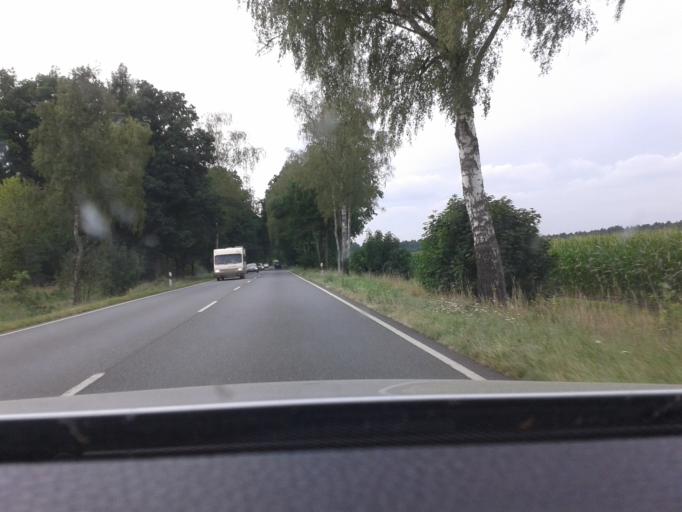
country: DE
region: Lower Saxony
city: Leiferde
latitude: 52.4788
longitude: 10.4527
